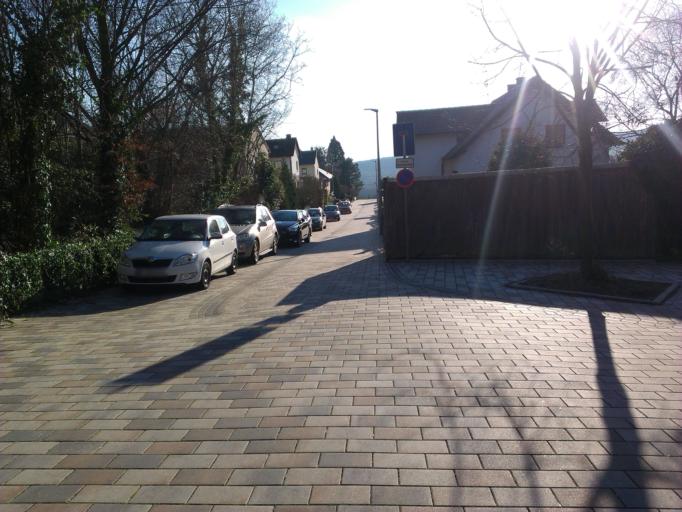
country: DE
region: Rheinland-Pfalz
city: Molsheim
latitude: 49.6461
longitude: 8.1712
